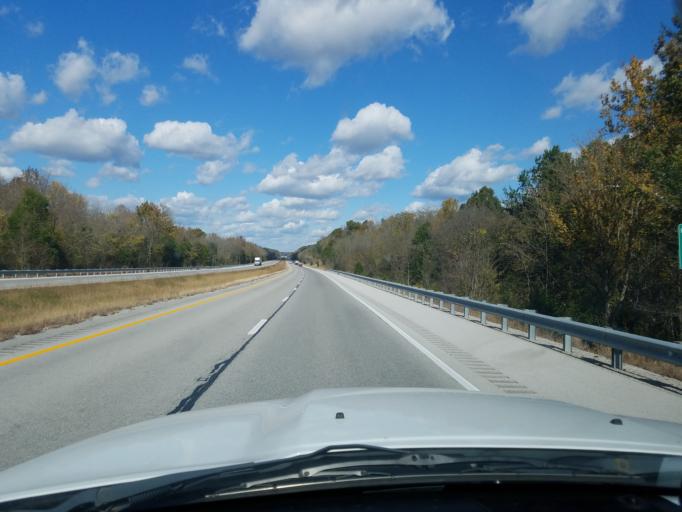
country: US
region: Kentucky
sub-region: Butler County
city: Morgantown
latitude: 37.1224
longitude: -86.6430
